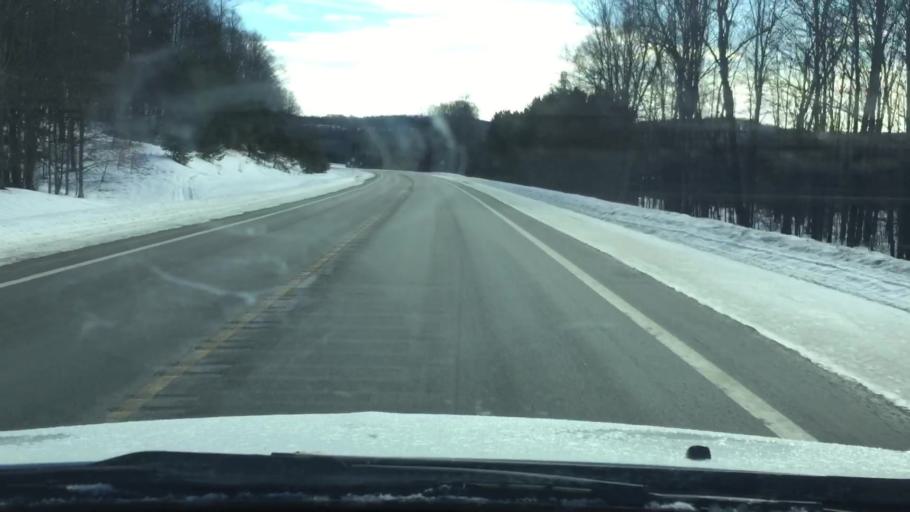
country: US
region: Michigan
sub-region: Antrim County
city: Mancelona
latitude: 44.9723
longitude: -85.0550
